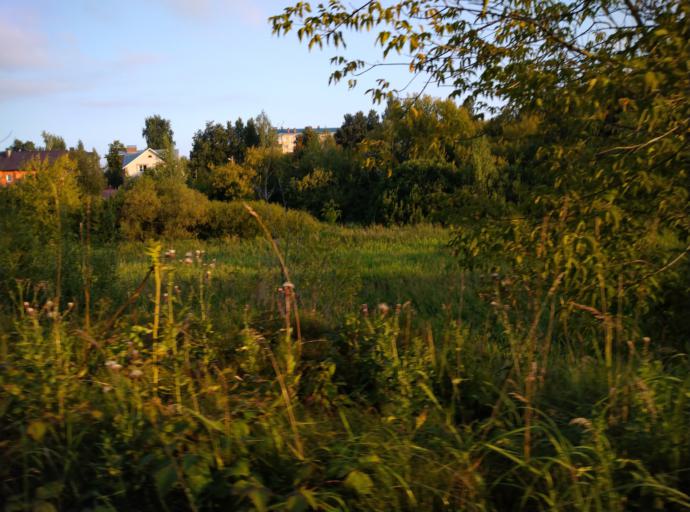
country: RU
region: Kostroma
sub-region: Kostromskoy Rayon
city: Kostroma
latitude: 57.7509
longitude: 40.9586
